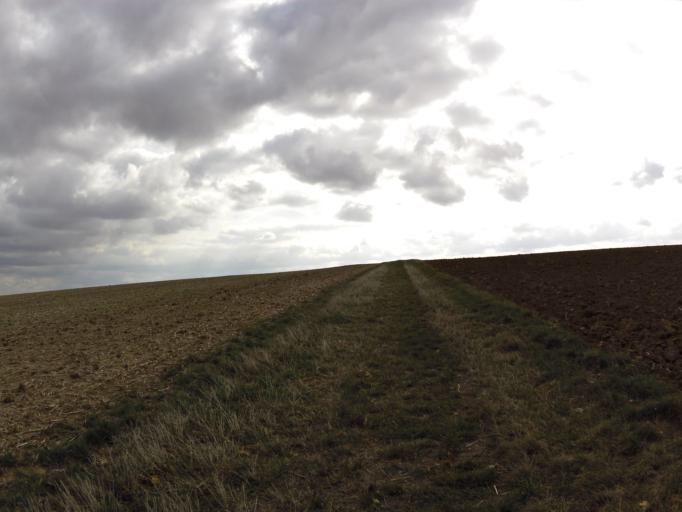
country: DE
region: Bavaria
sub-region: Regierungsbezirk Unterfranken
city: Reichenberg
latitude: 49.7033
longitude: 9.9420
